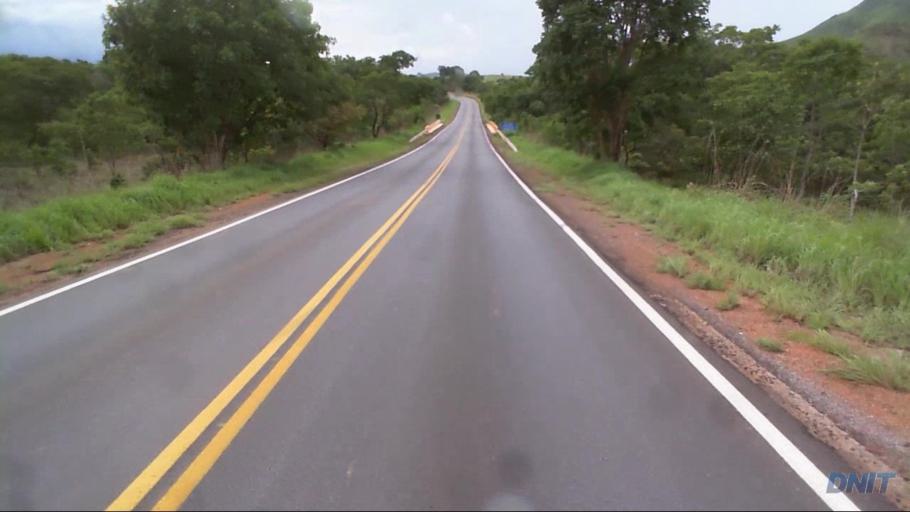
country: BR
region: Goias
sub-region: Padre Bernardo
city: Padre Bernardo
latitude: -15.4111
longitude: -48.2005
